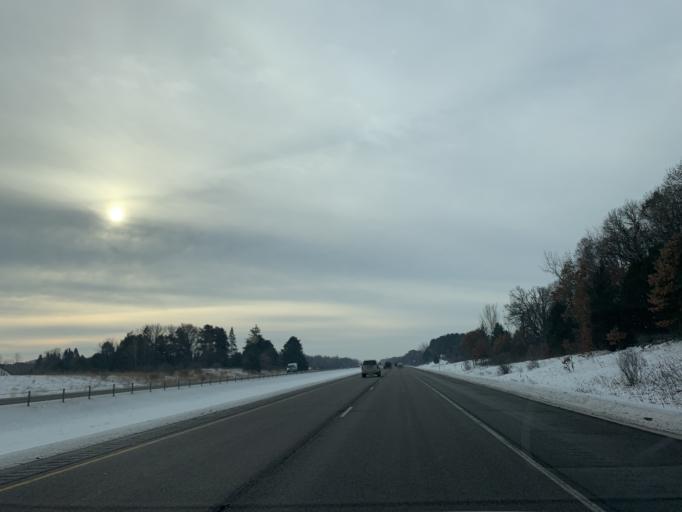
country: US
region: Minnesota
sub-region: Chisago County
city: Wyoming
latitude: 45.3175
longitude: -93.0037
